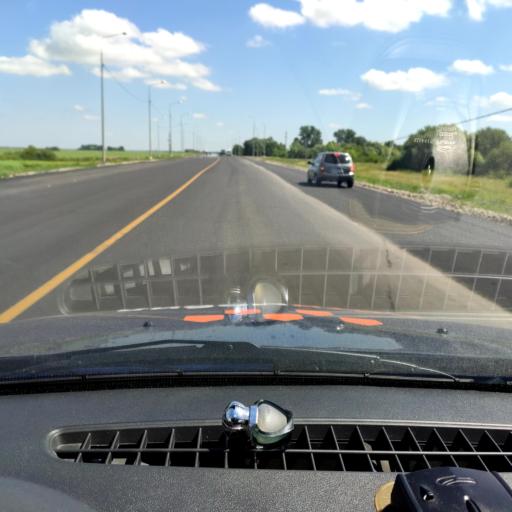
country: RU
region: Orjol
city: Zmiyevka
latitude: 52.7002
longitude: 36.3761
